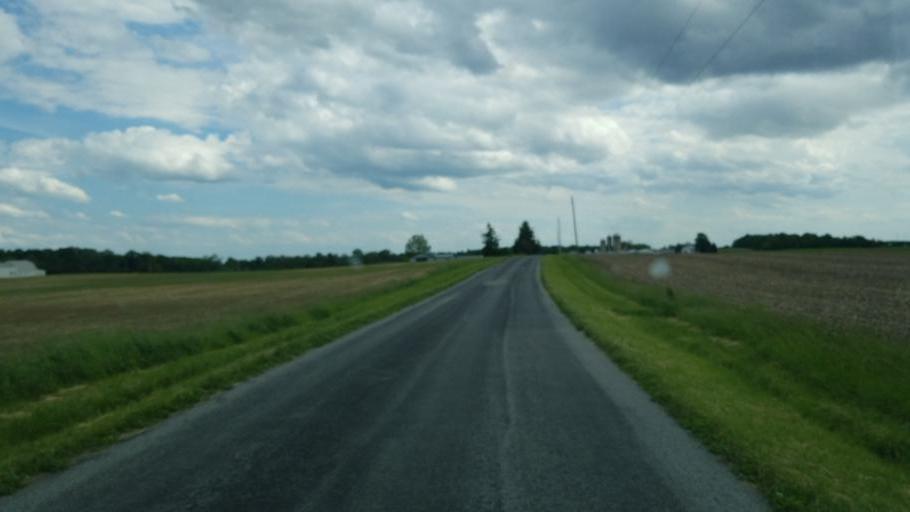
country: US
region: Ohio
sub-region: Huron County
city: Plymouth
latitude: 40.9558
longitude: -82.6383
